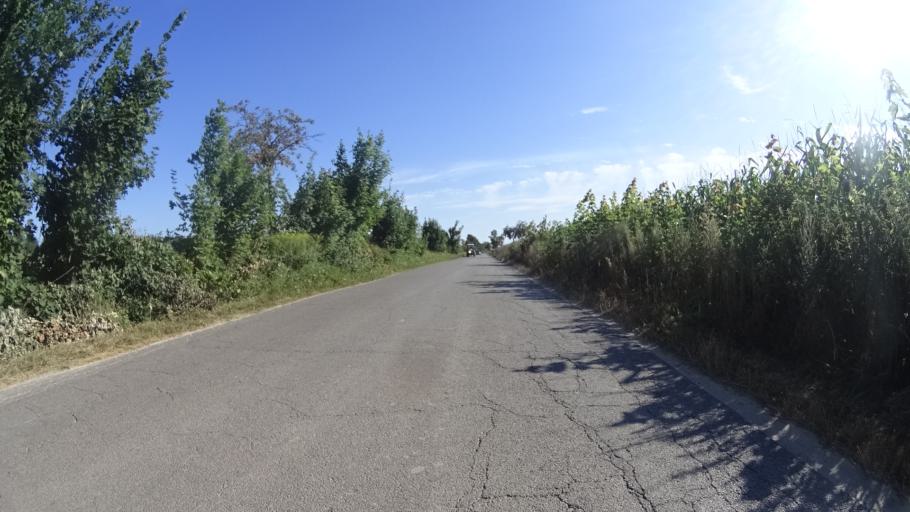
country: PL
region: Masovian Voivodeship
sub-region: Powiat bialobrzeski
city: Wysmierzyce
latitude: 51.6699
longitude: 20.8312
